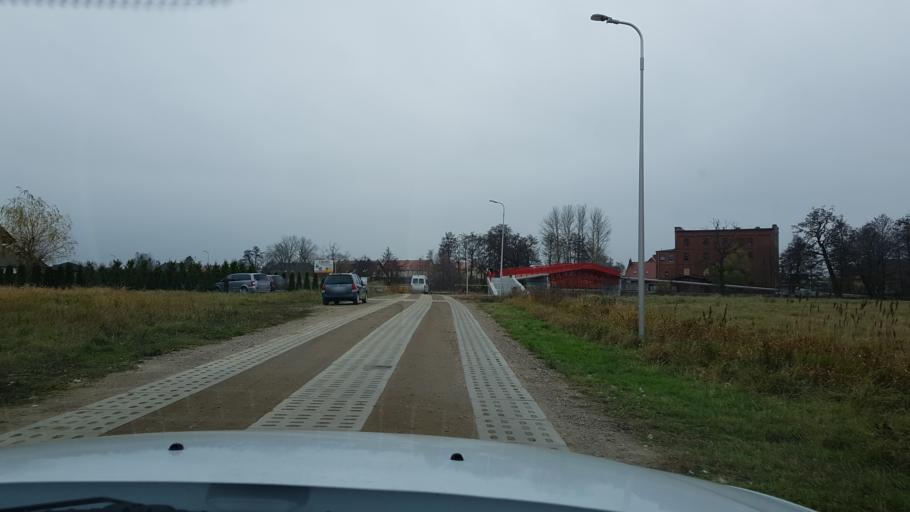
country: PL
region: West Pomeranian Voivodeship
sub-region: Powiat slawienski
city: Darlowo
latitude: 54.4169
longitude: 16.4162
